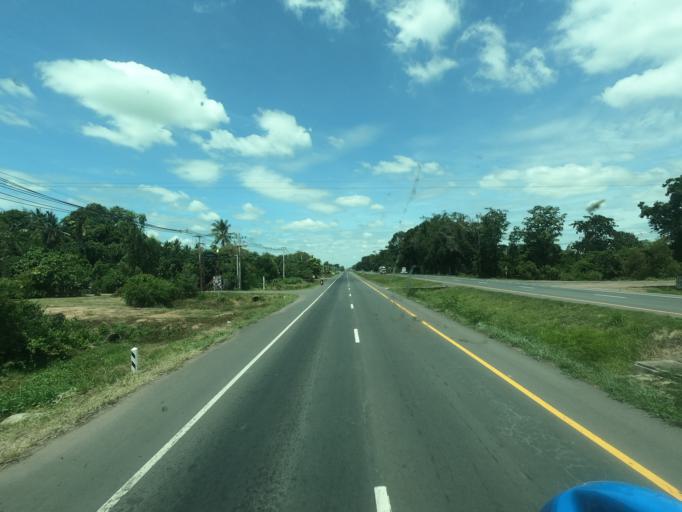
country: TH
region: Surin
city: Prasat
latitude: 14.6204
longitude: 103.3697
